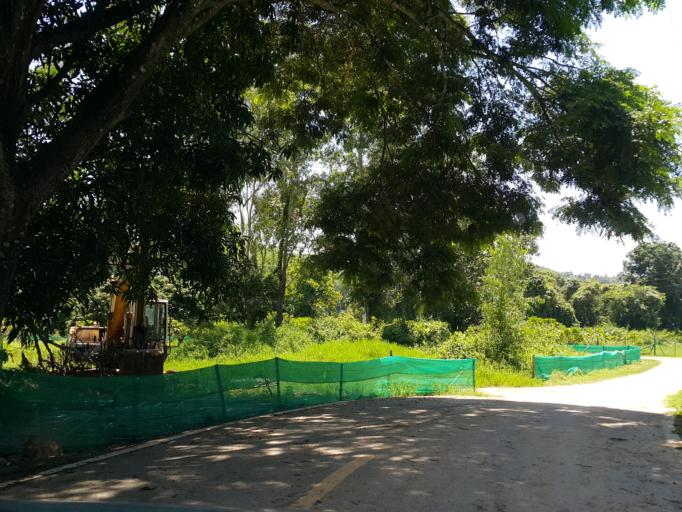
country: TH
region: Lamphun
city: Ban Thi
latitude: 18.6841
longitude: 99.1694
